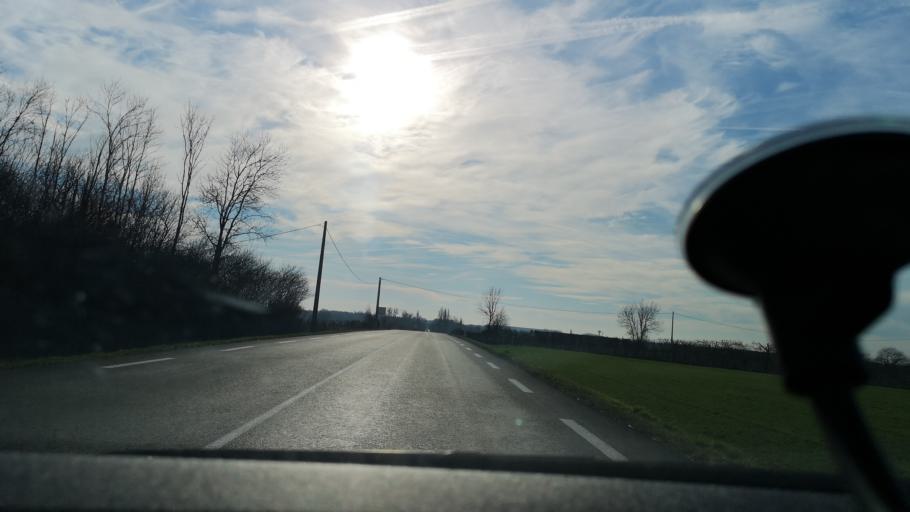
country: FR
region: Bourgogne
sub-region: Departement de la Cote-d'Or
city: Seurre
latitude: 46.9499
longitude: 5.1576
